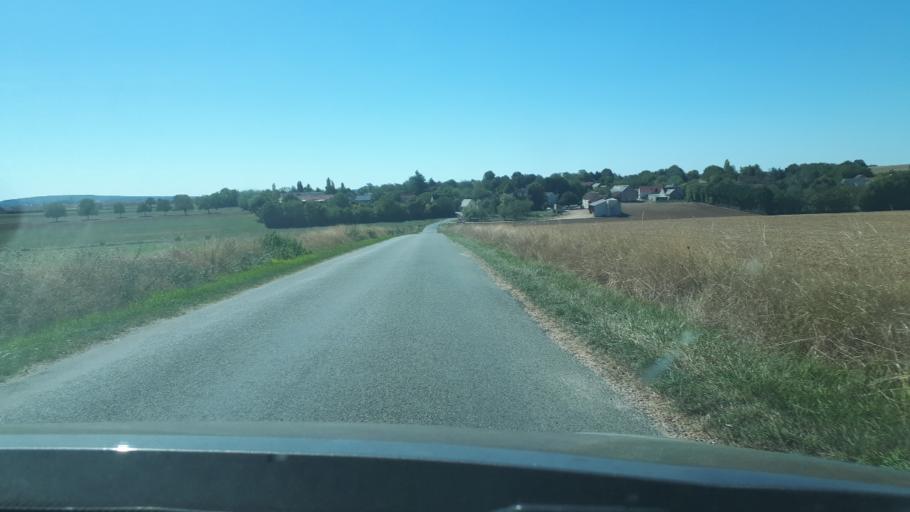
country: FR
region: Centre
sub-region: Departement du Cher
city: Baugy
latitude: 47.2123
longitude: 2.7458
